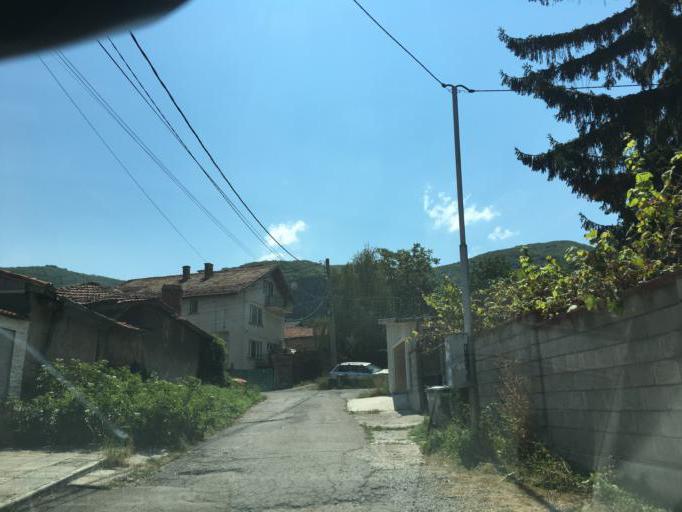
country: BG
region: Sofiya
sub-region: Obshtina Elin Pelin
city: Elin Pelin
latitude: 42.6031
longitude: 23.4711
